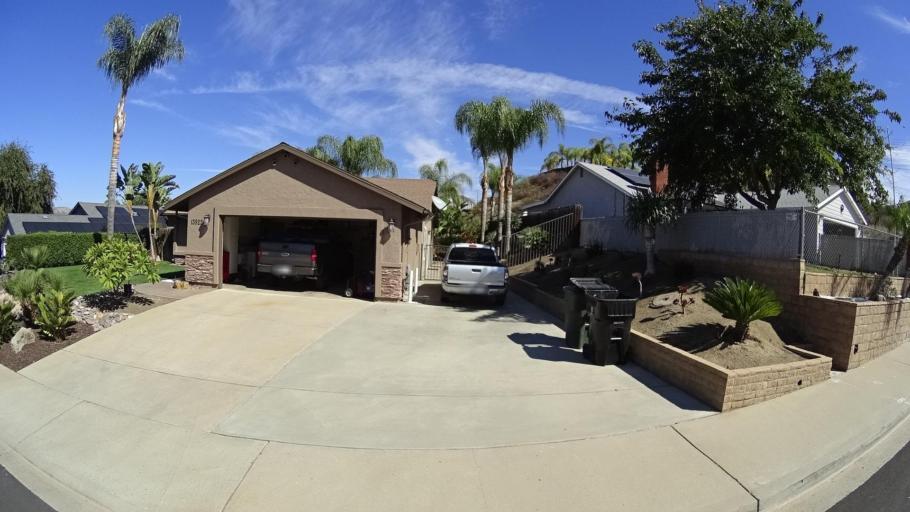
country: US
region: California
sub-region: San Diego County
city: Crest
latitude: 32.8328
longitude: -116.8888
